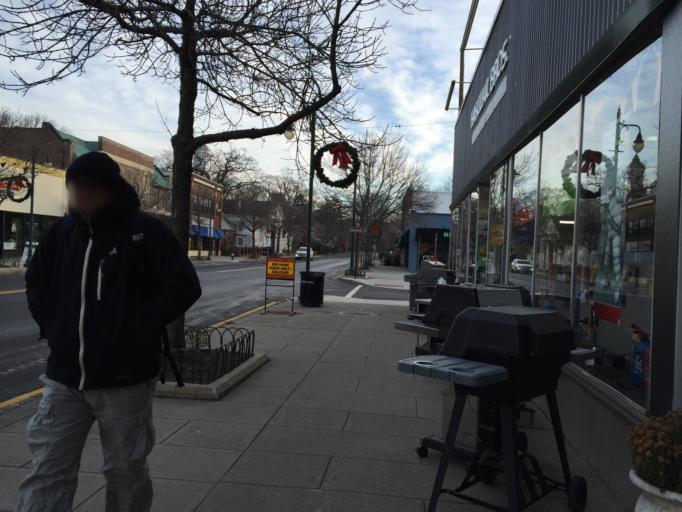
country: US
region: New Jersey
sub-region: Union County
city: Summit
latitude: 40.7181
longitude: -74.3556
